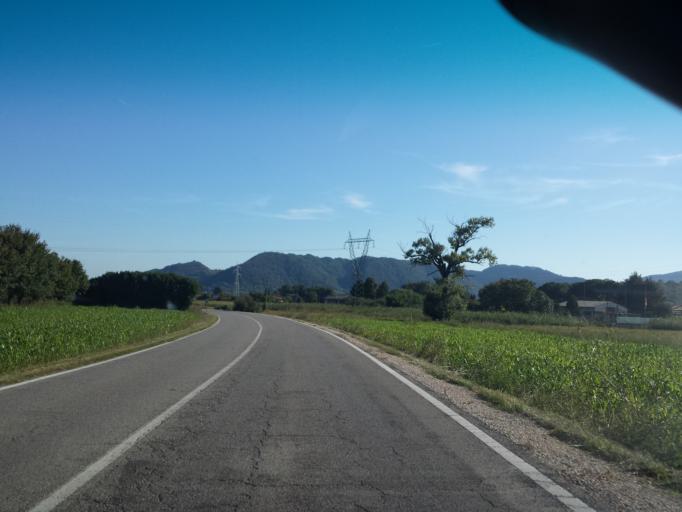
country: IT
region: Veneto
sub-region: Provincia di Vicenza
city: San Vito di Leguzzano
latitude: 45.6762
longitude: 11.3864
